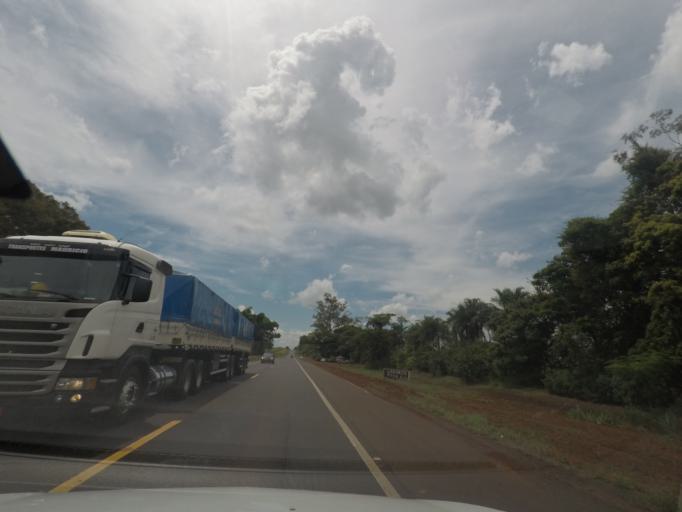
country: BR
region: Sao Paulo
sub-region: Barretos
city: Barretos
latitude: -20.3671
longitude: -48.6466
